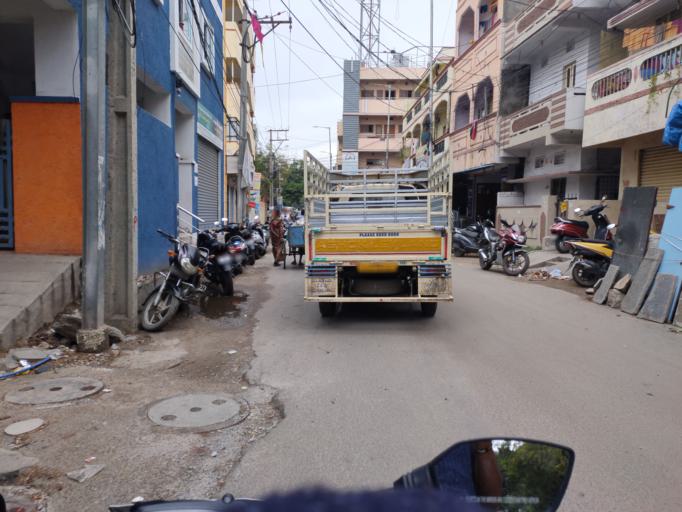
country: IN
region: Telangana
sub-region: Rangareddi
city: Kukatpalli
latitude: 17.4493
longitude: 78.4470
